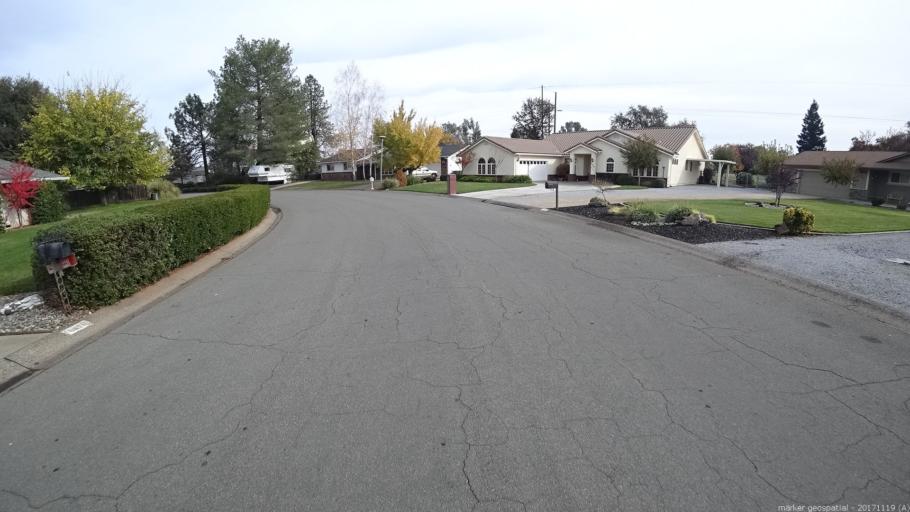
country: US
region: California
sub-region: Shasta County
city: Anderson
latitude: 40.4880
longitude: -122.3067
